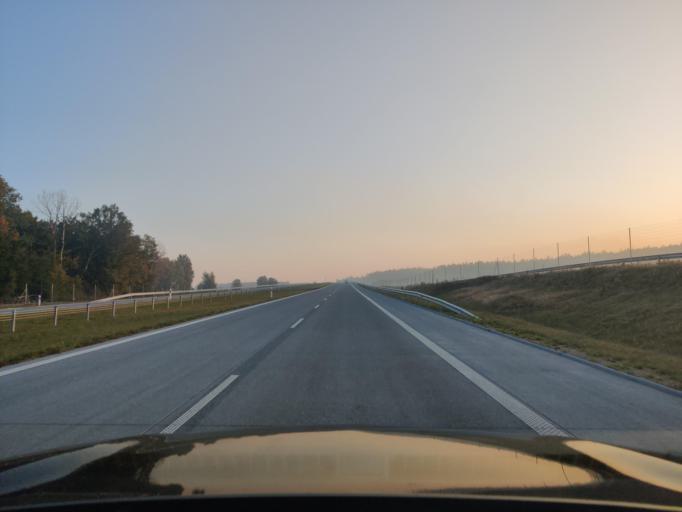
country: PL
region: Masovian Voivodeship
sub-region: Powiat mlawski
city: Wisniewo
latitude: 52.9764
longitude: 20.3312
